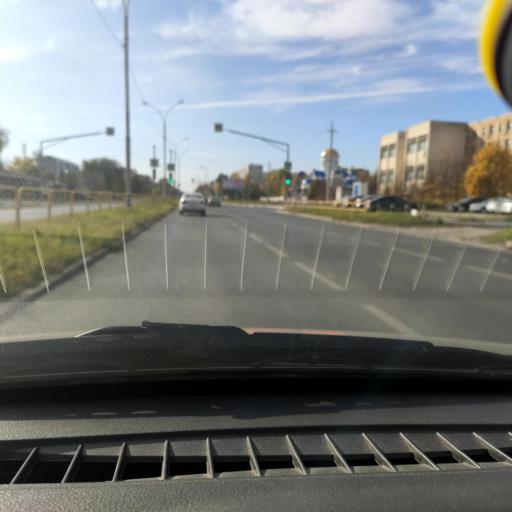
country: RU
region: Samara
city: Tol'yatti
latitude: 53.5370
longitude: 49.3145
